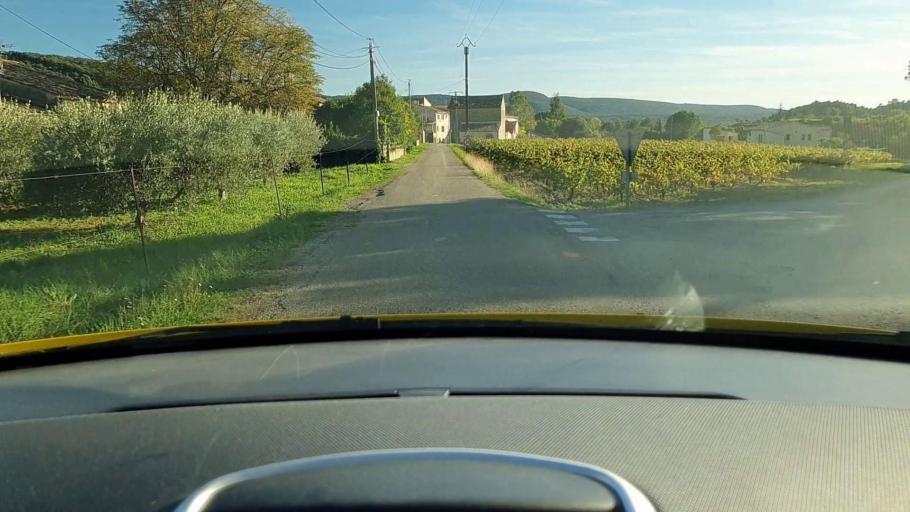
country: FR
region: Languedoc-Roussillon
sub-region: Departement du Gard
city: Saint-Hippolyte-du-Fort
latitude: 43.9586
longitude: 3.8067
